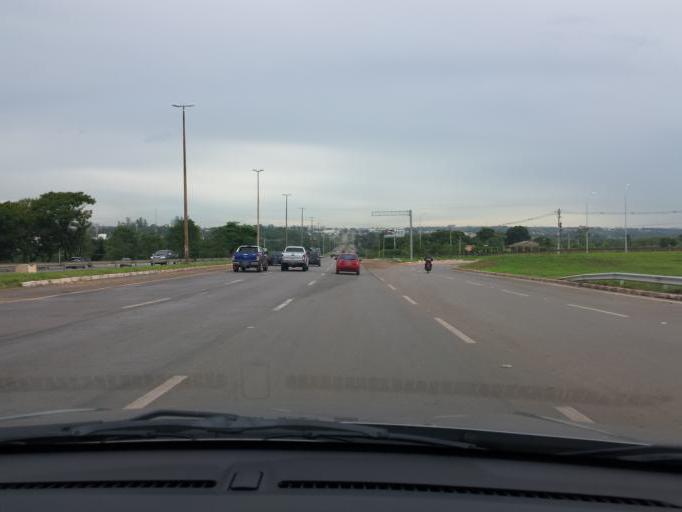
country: BR
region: Federal District
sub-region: Brasilia
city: Brasilia
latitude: -15.8744
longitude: -47.9586
